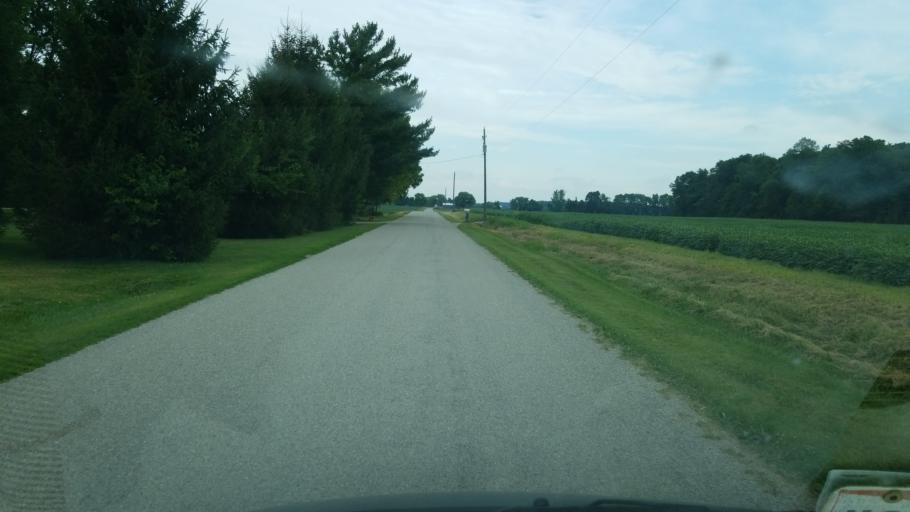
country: US
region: Ohio
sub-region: Seneca County
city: Tiffin
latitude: 41.0247
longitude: -83.0546
